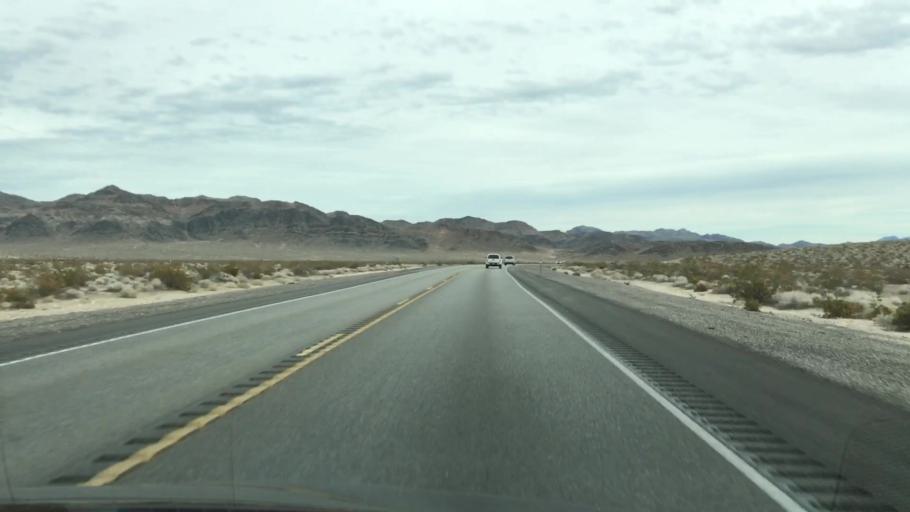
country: US
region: Nevada
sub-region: Nye County
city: Beatty
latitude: 36.6316
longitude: -116.3240
